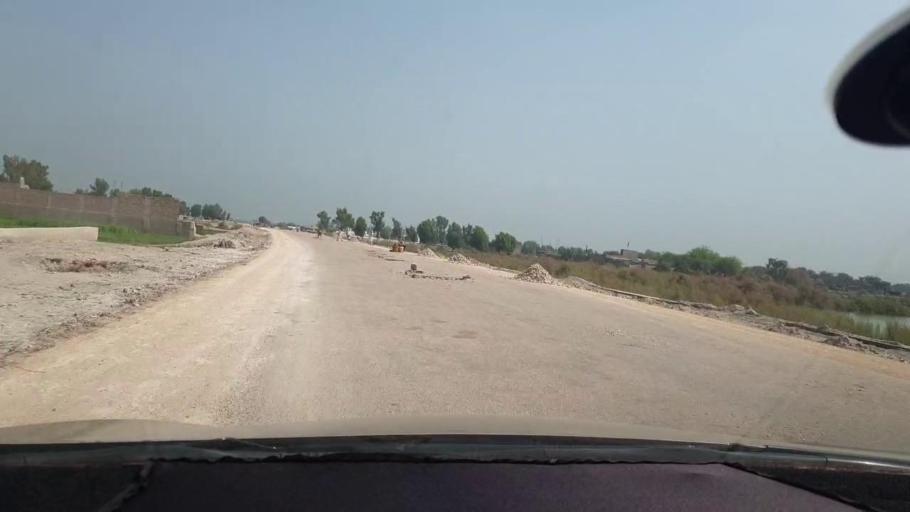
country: PK
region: Sindh
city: Kambar
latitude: 27.5845
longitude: 68.0246
